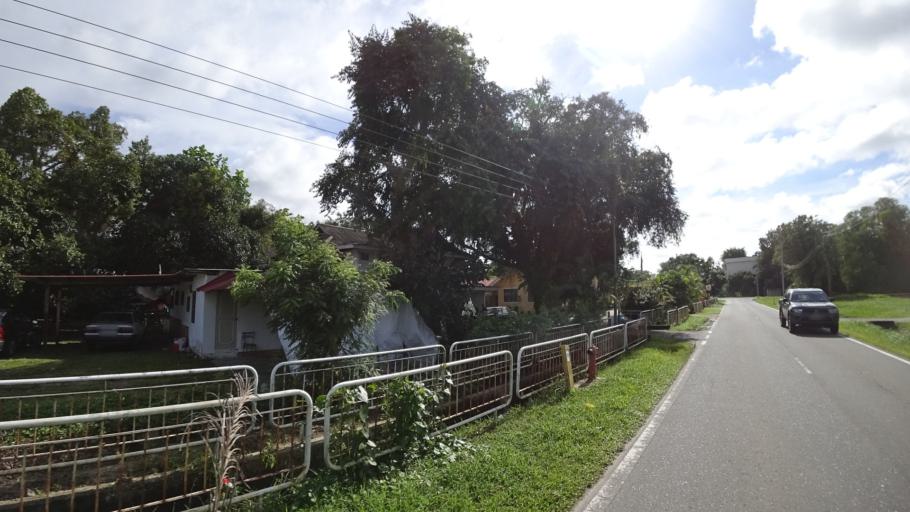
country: BN
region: Brunei and Muara
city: Bandar Seri Begawan
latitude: 4.9367
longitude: 114.9457
